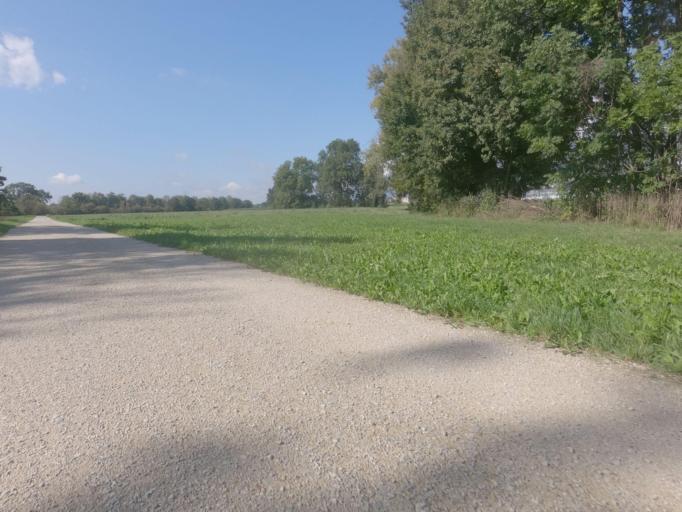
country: CH
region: Solothurn
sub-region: Bezirk Olten
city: Wangen
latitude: 47.3349
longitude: 7.8612
